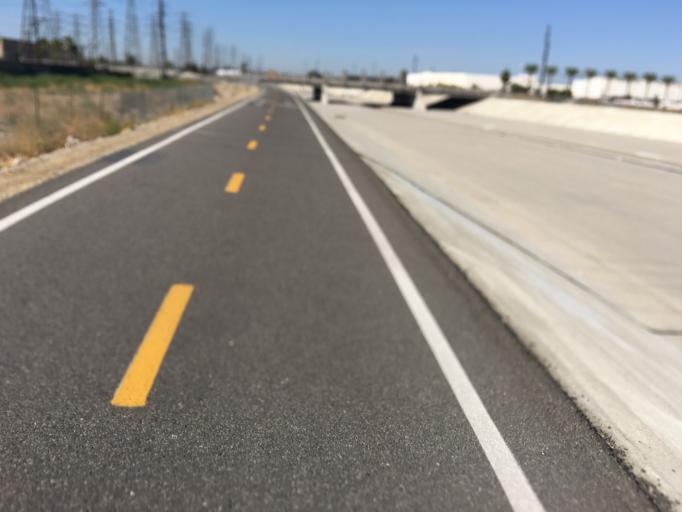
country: US
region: California
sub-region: Los Angeles County
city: Downey
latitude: 33.9293
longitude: -118.1076
